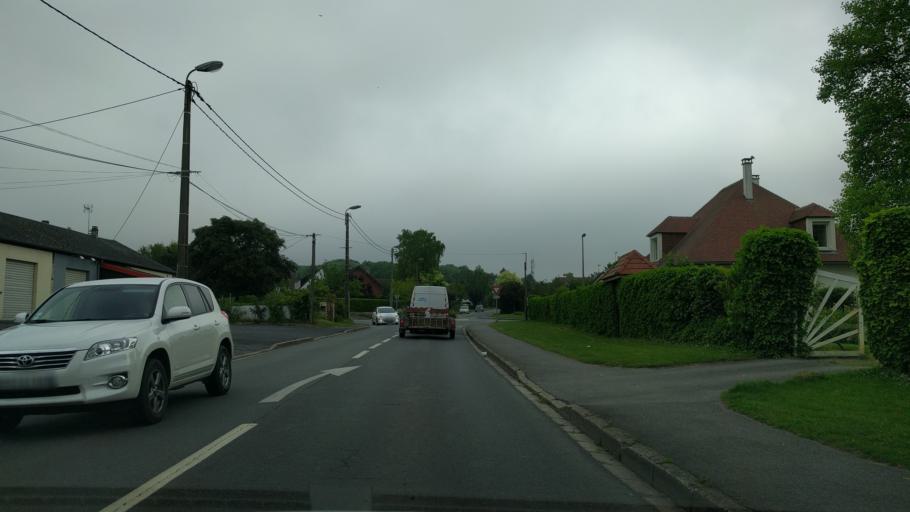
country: FR
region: Picardie
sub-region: Departement de la Somme
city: Peronne
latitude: 49.9420
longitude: 2.9341
